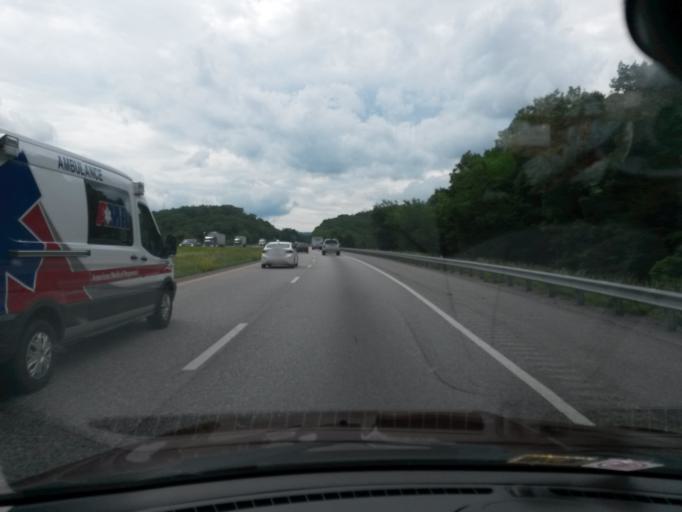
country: US
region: Virginia
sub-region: Alleghany County
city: Clifton Forge
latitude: 37.8296
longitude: -79.8098
